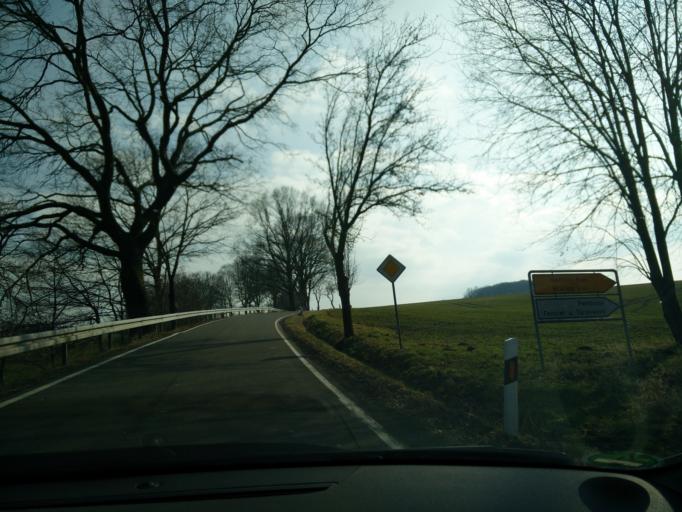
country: DE
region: Saxony
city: Colditz
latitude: 51.1109
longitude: 12.8167
